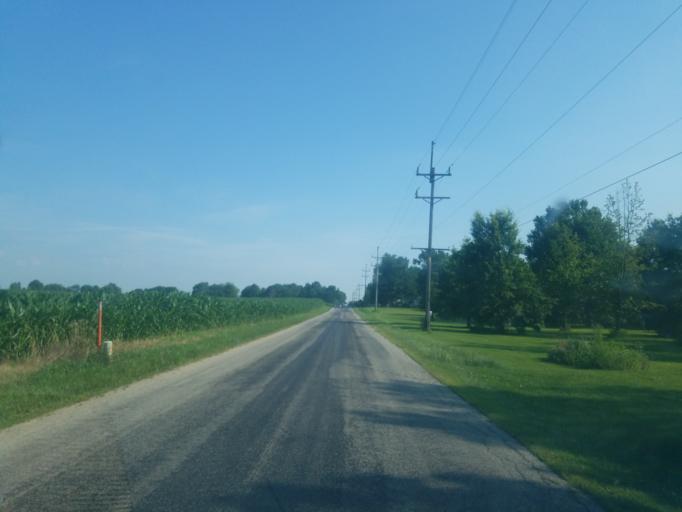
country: US
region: Ohio
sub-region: Huron County
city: Plymouth
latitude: 40.9475
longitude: -82.6862
